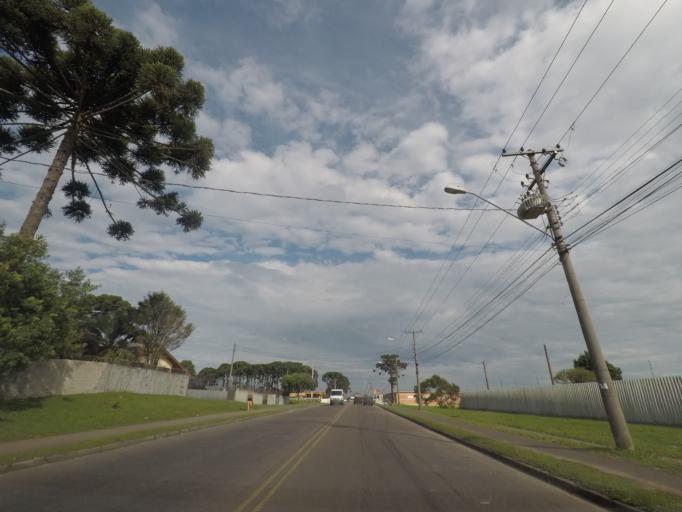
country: BR
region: Parana
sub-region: Sao Jose Dos Pinhais
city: Sao Jose dos Pinhais
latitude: -25.5452
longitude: -49.2940
